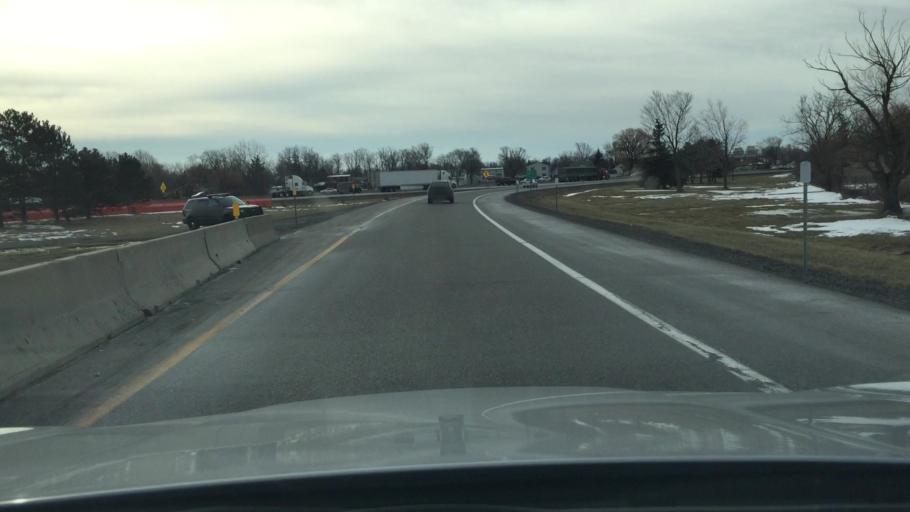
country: US
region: New York
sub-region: Erie County
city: Cheektowaga
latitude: 42.9308
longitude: -78.7683
